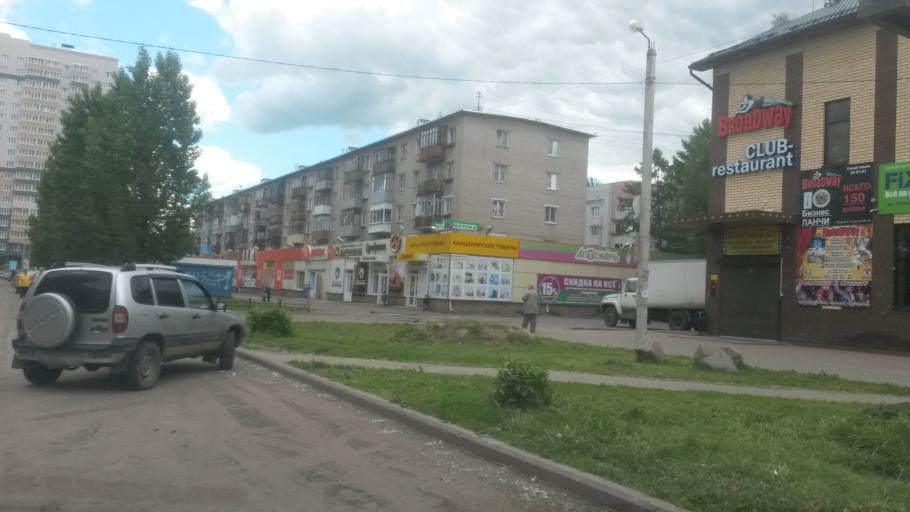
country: RU
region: Jaroslavl
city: Yaroslavl
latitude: 57.6853
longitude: 39.8029
